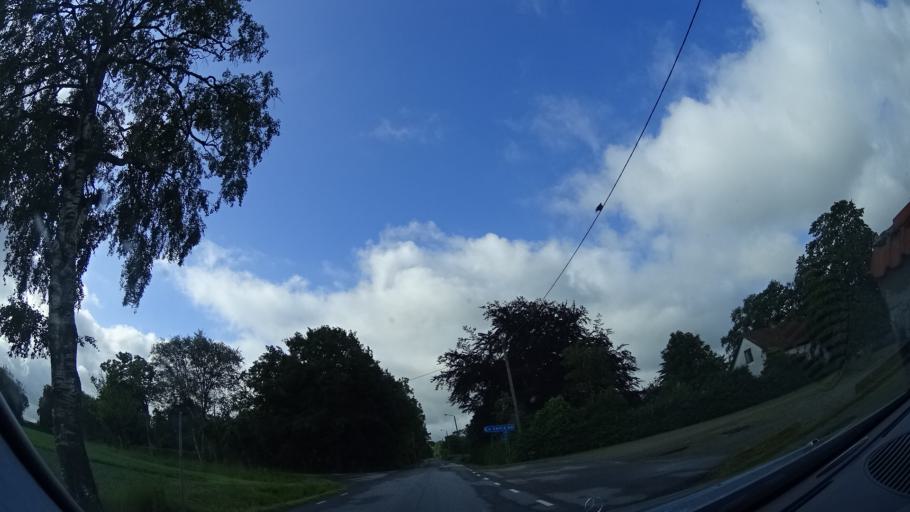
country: SE
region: Skane
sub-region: Eslovs Kommun
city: Stehag
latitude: 55.8961
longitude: 13.4156
